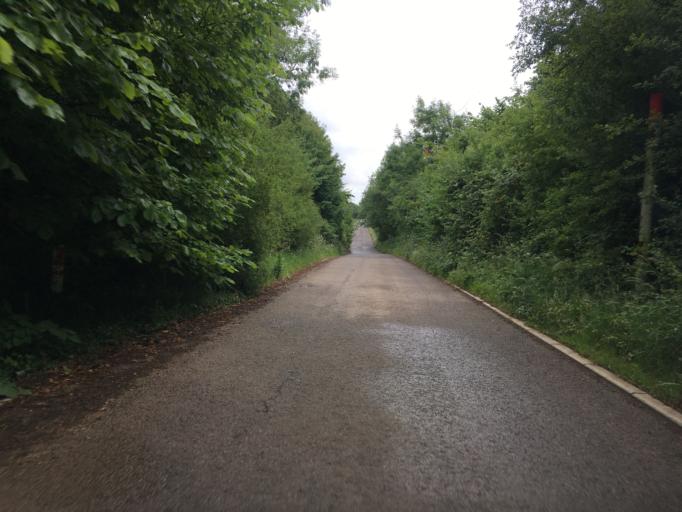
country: GB
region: England
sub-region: Gloucestershire
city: Charlton Kings
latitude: 51.7981
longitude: -2.0532
